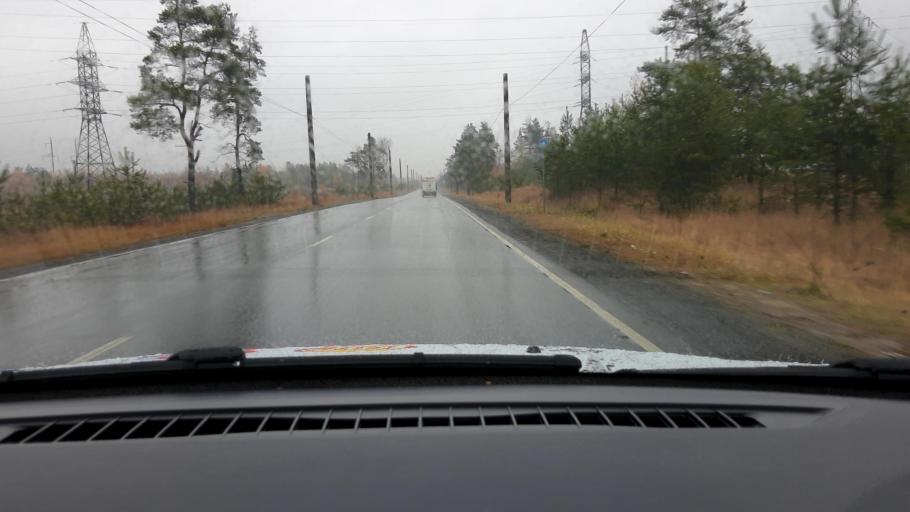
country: RU
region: Nizjnij Novgorod
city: Dzerzhinsk
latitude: 56.2669
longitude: 43.5338
